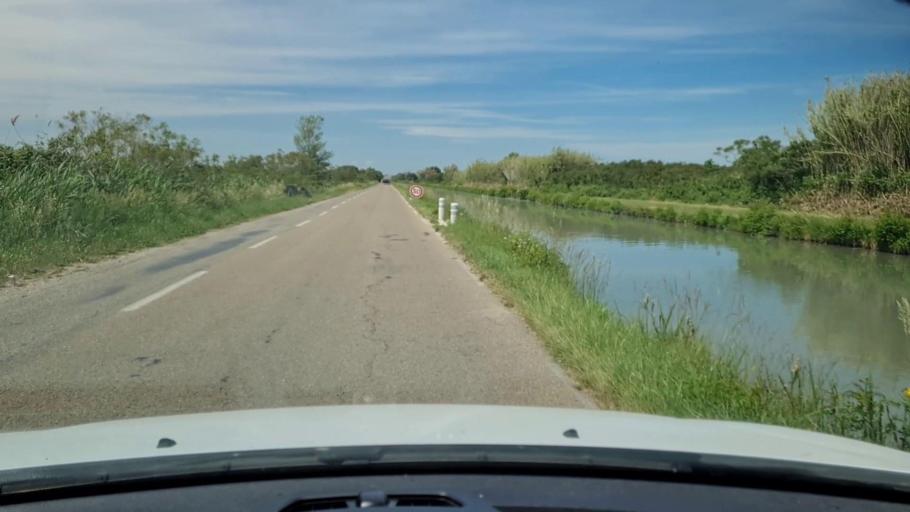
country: FR
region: Languedoc-Roussillon
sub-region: Departement du Gard
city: Vauvert
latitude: 43.5951
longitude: 4.3418
